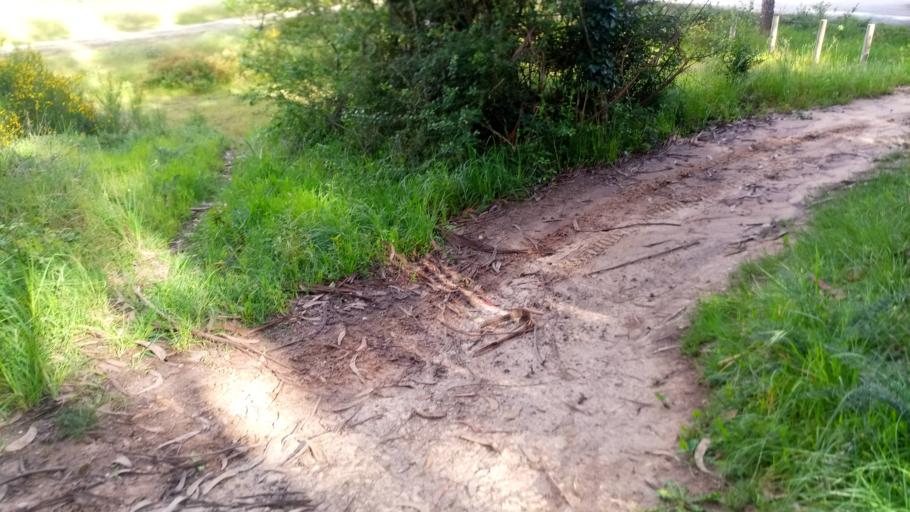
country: PT
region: Leiria
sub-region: Obidos
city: Obidos
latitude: 39.3906
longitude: -9.2010
